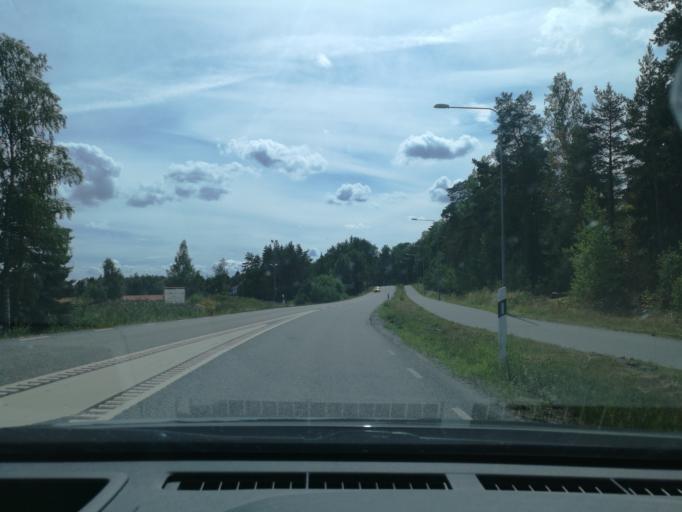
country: SE
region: Stockholm
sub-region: Sigtuna Kommun
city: Rosersberg
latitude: 59.6023
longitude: 17.8825
